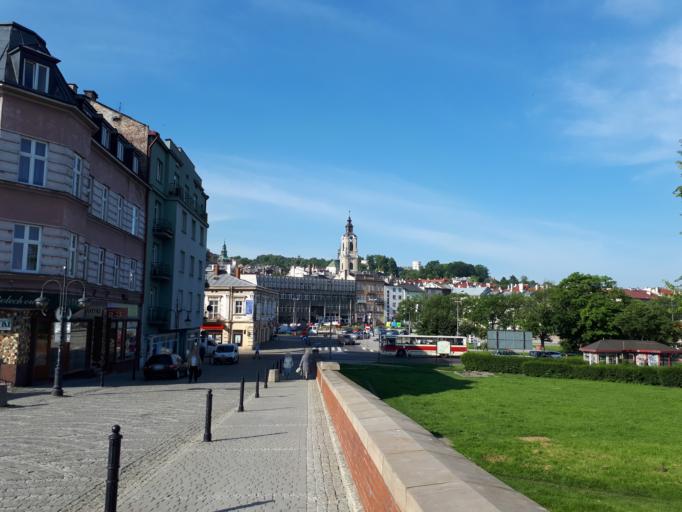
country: PL
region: Subcarpathian Voivodeship
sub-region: Przemysl
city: Przemysl
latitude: 49.7844
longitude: 22.7724
